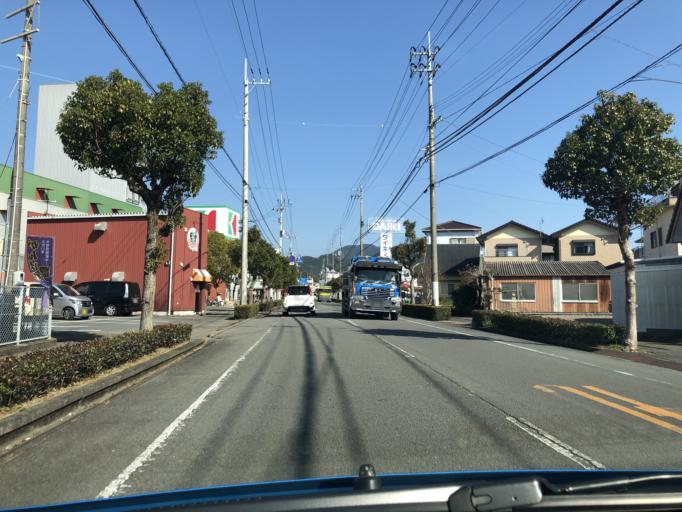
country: JP
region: Kochi
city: Sukumo
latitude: 32.9359
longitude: 132.7209
